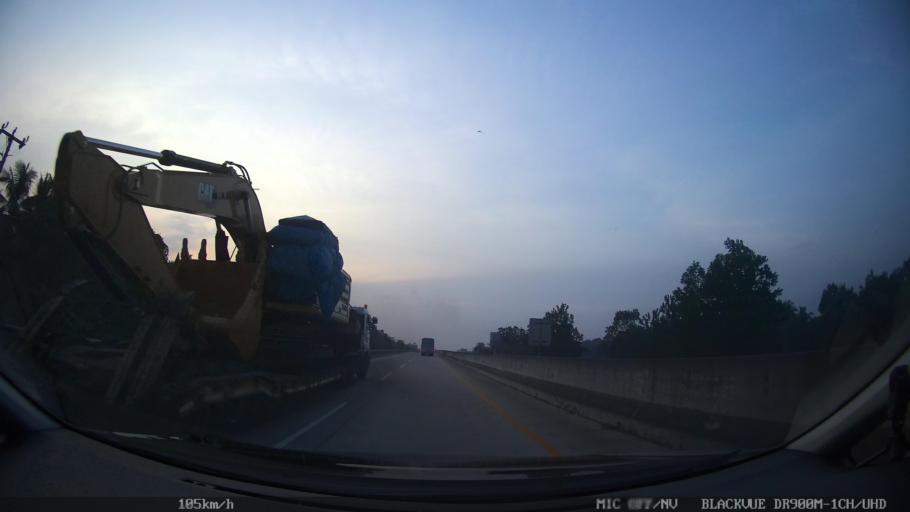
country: ID
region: Lampung
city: Pasuruan
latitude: -5.7096
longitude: 105.6456
